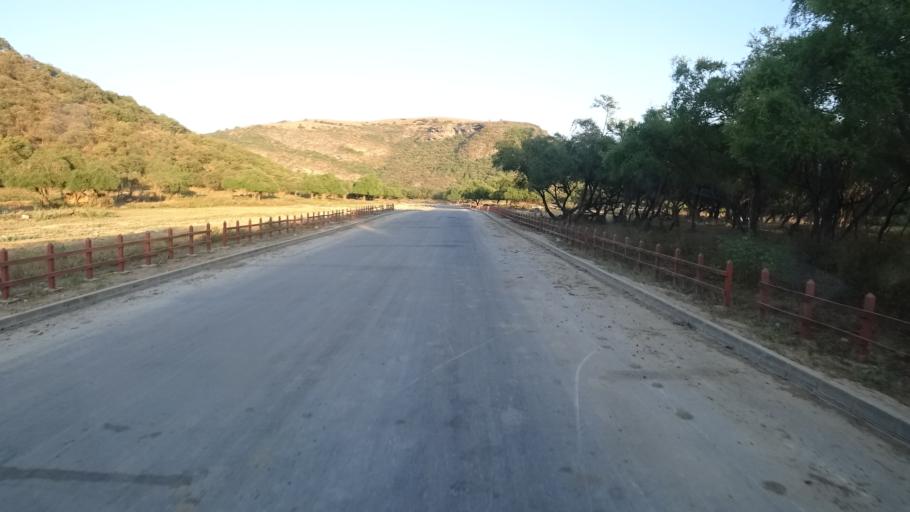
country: OM
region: Zufar
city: Salalah
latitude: 17.0906
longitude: 54.4406
